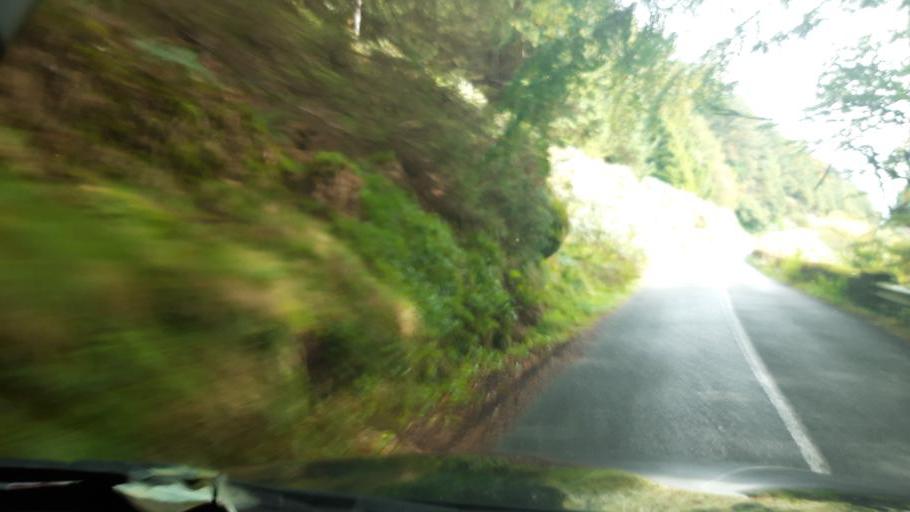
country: IE
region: Leinster
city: Ballinteer
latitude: 53.2311
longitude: -6.2723
